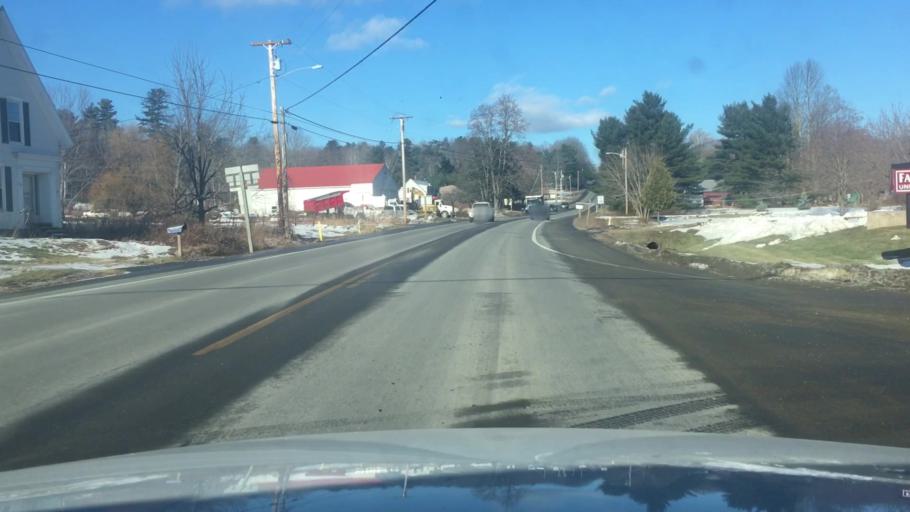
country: US
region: Maine
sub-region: Kennebec County
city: Waterville
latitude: 44.6069
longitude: -69.6626
